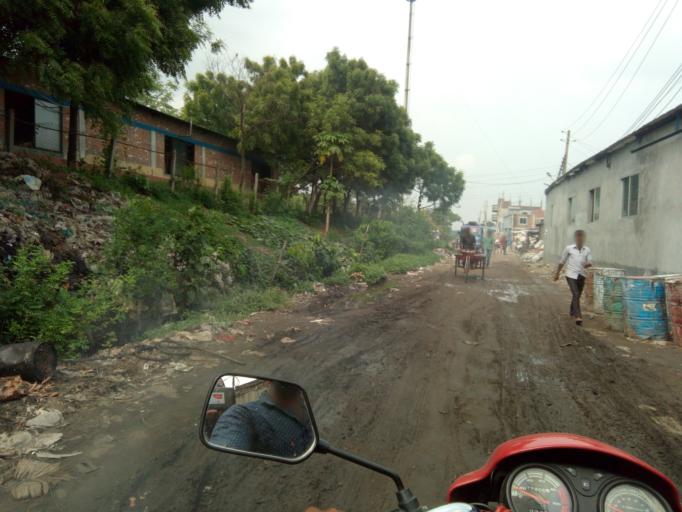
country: BD
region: Dhaka
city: Paltan
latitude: 23.7157
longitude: 90.4498
